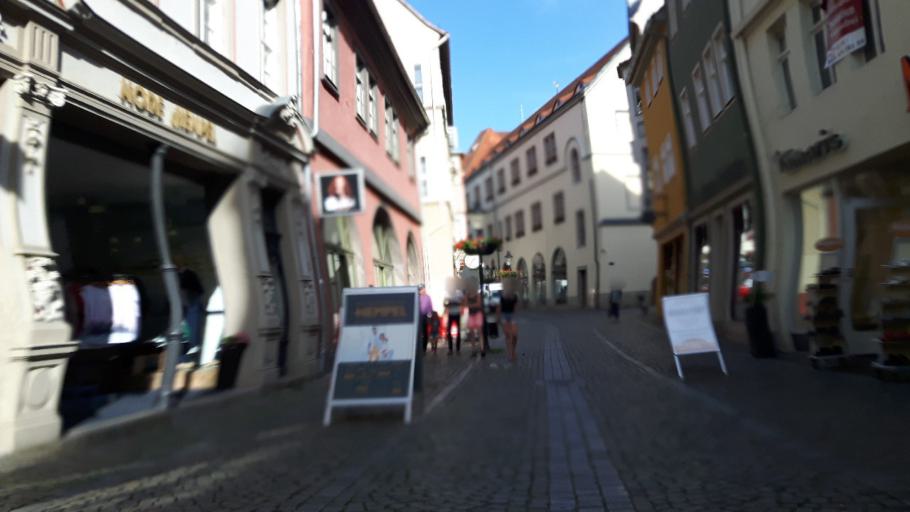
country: DE
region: Saxony-Anhalt
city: Naumburg
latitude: 51.1532
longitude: 11.8080
